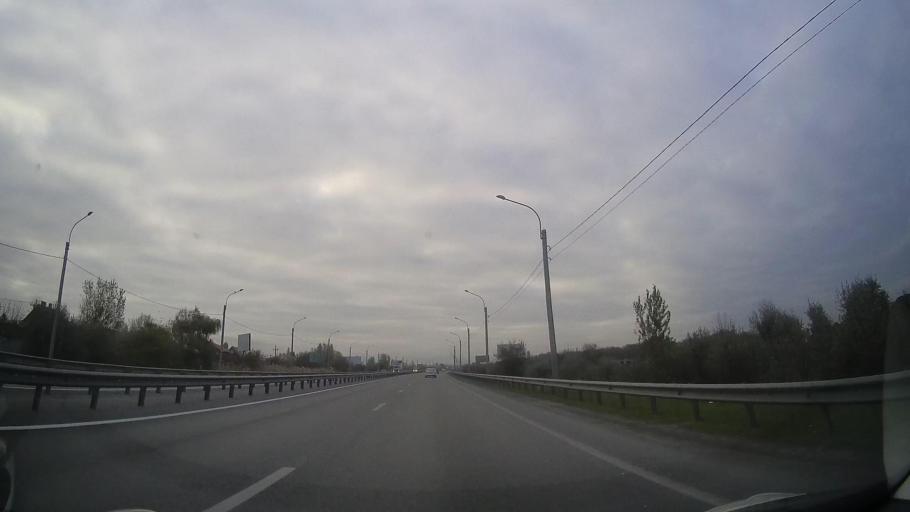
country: RU
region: Rostov
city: Bataysk
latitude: 47.1494
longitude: 39.7733
